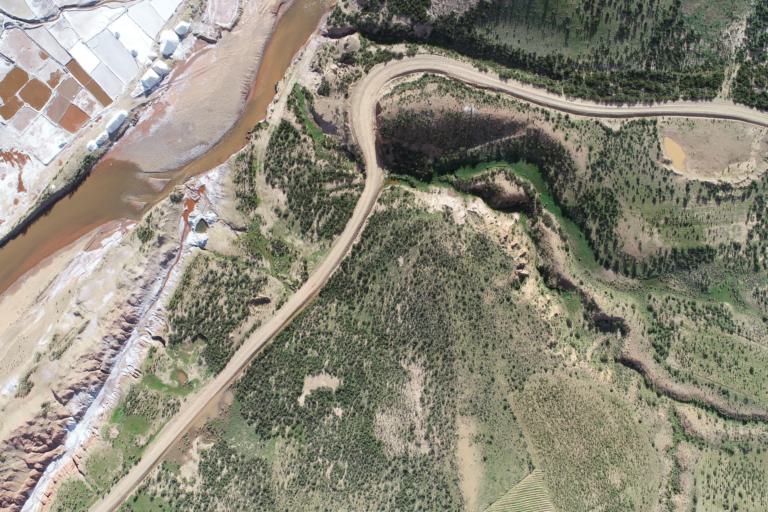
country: BO
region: La Paz
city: Patacamaya
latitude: -17.2981
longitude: -68.4858
